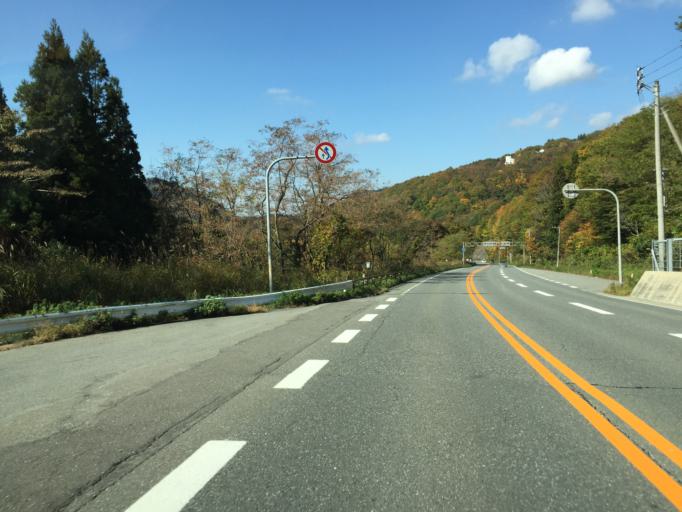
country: JP
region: Yamagata
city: Yonezawa
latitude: 37.8536
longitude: 140.2391
